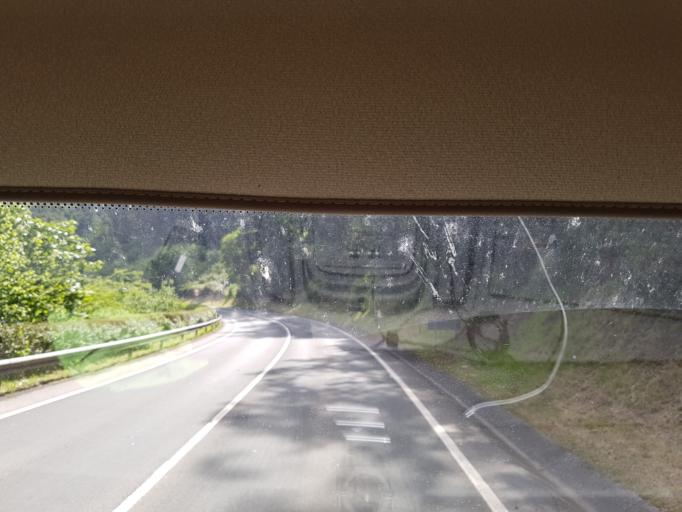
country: ES
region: Basque Country
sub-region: Bizkaia
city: Sopuerta
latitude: 43.2837
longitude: -3.1374
